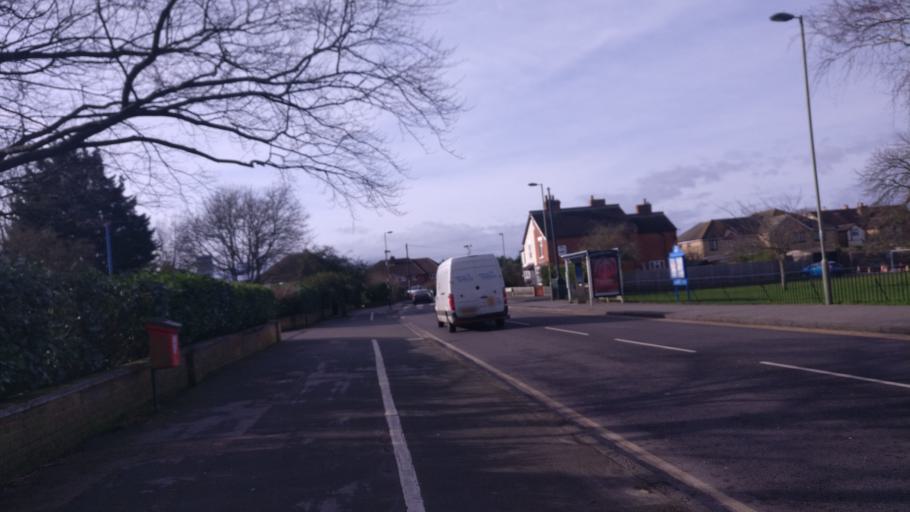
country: GB
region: England
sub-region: Surrey
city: Staines
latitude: 51.4285
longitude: -0.5229
